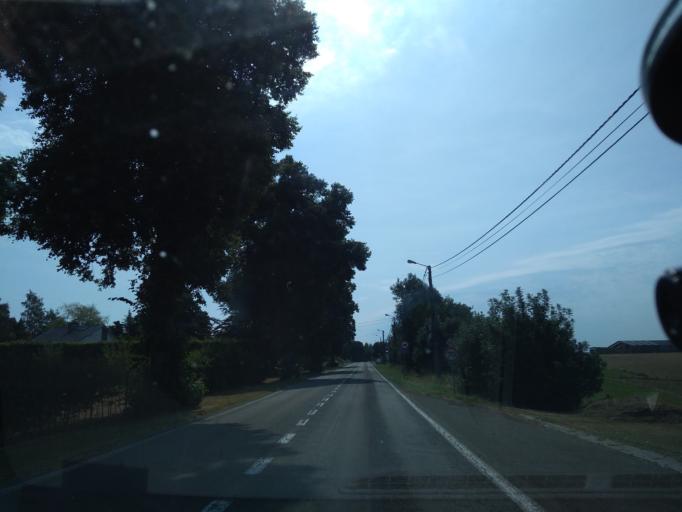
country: BE
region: Wallonia
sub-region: Province du Luxembourg
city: La Roche-en-Ardenne
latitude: 50.1684
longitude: 5.5536
